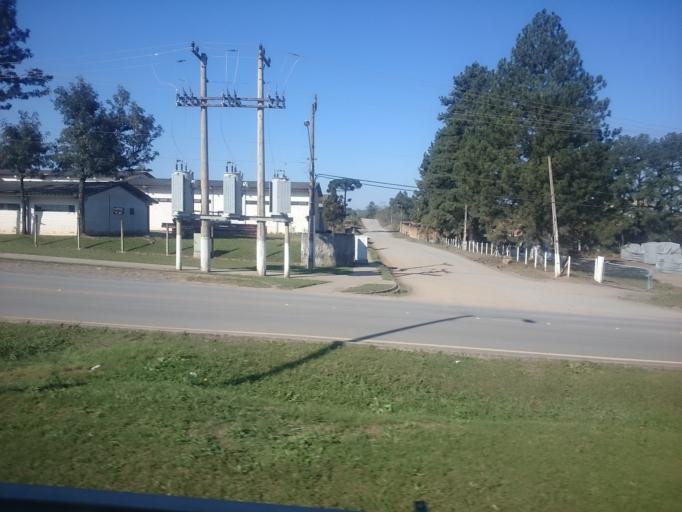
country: BR
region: Parana
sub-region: Rio Negro
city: Rio Negro
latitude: -26.0980
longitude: -49.7805
